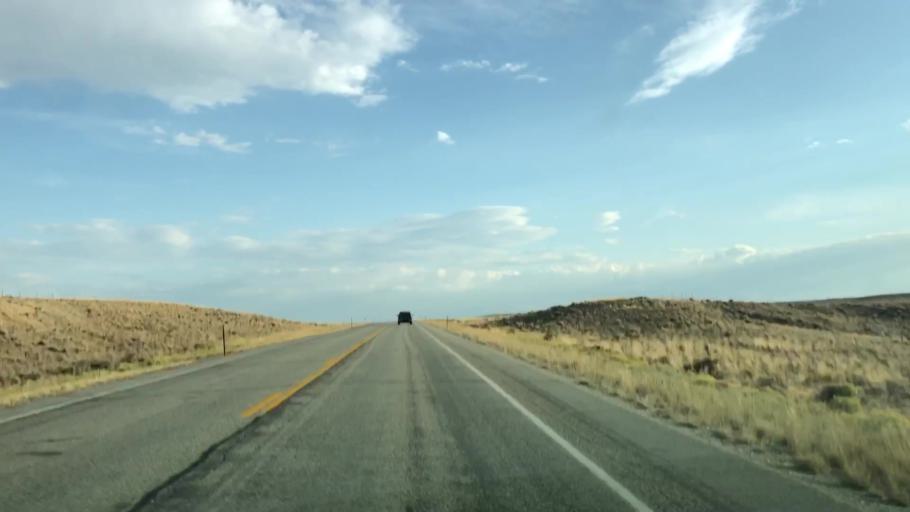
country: US
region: Wyoming
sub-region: Sublette County
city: Pinedale
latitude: 42.3453
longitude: -109.5220
